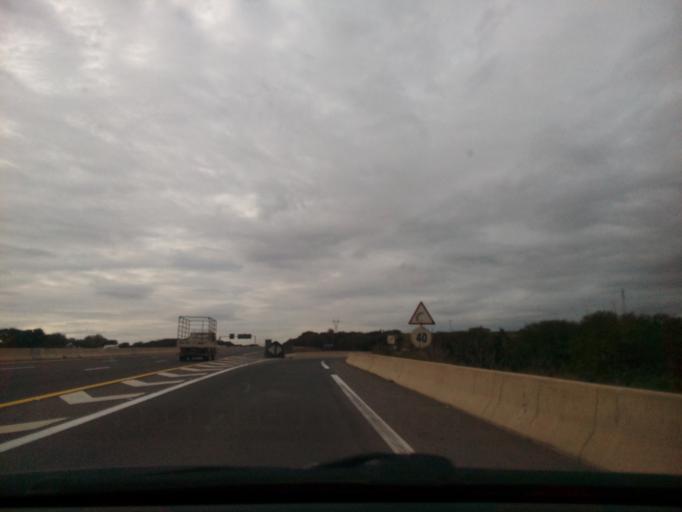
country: DZ
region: Oran
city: Sidi ech Chahmi
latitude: 35.5442
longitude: -0.3791
